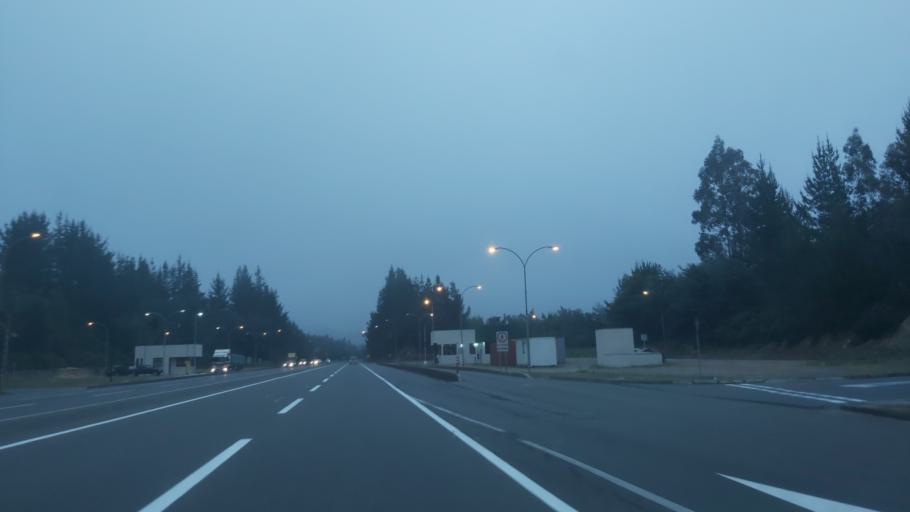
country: CL
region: Biobio
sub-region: Provincia de Concepcion
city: Penco
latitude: -36.7351
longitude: -72.8875
